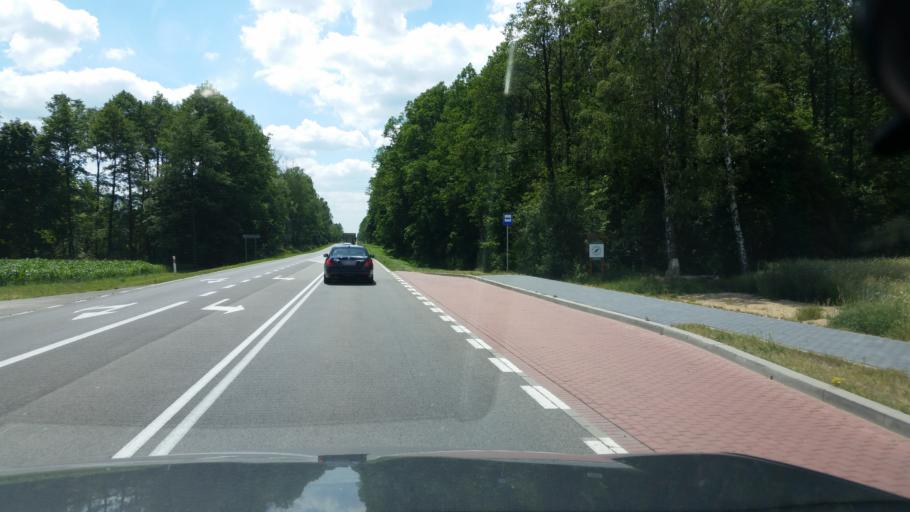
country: PL
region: Masovian Voivodeship
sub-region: Powiat ostrowski
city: Ostrow Mazowiecka
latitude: 52.8994
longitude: 21.8701
